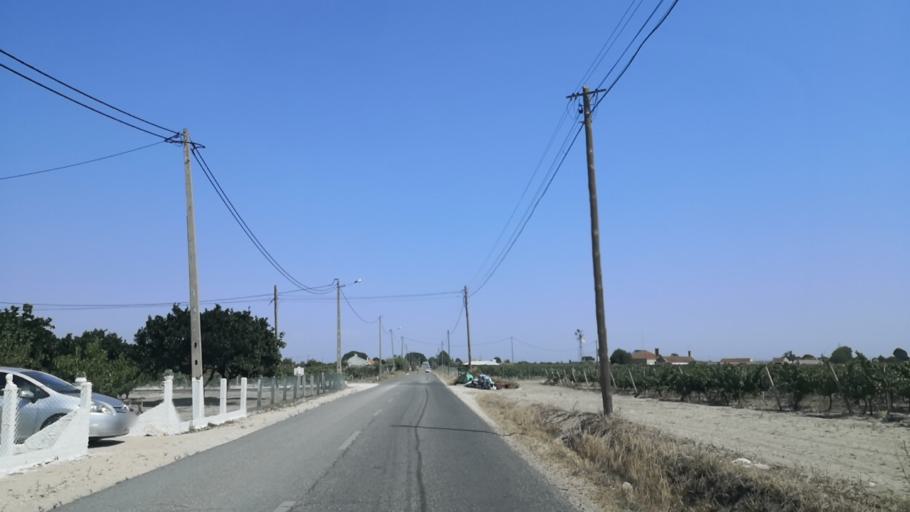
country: PT
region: Setubal
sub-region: Palmela
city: Palmela
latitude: 38.6057
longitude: -8.8393
